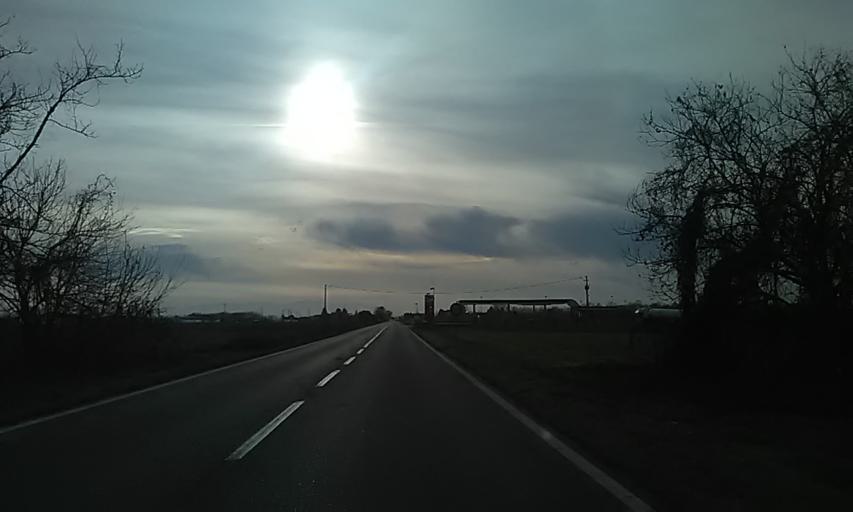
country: IT
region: Piedmont
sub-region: Provincia di Torino
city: Villareggia
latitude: 45.2814
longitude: 7.9884
